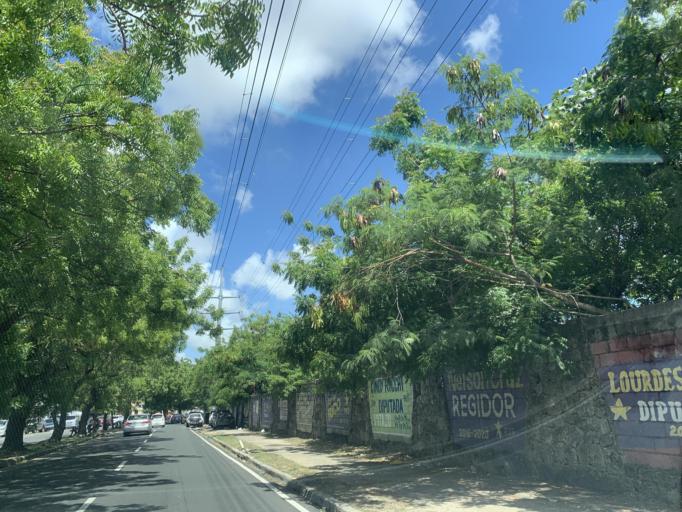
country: DO
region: Nacional
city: La Agustina
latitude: 18.5056
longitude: -69.9243
